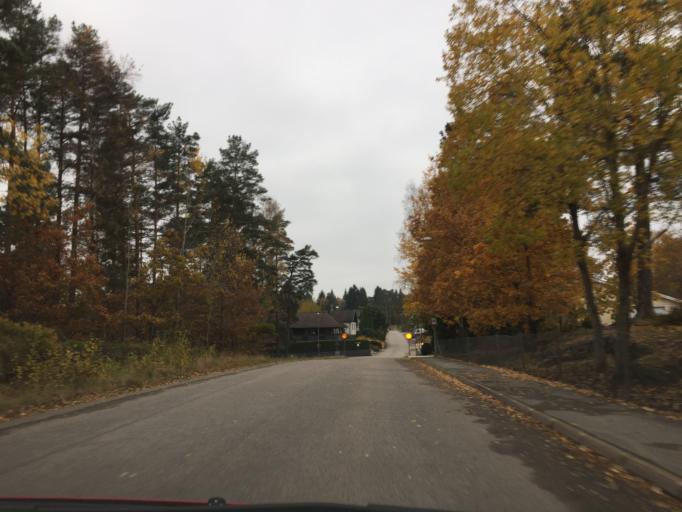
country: SE
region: Vaestra Goetaland
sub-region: Trollhattan
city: Trollhattan
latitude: 58.2604
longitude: 12.2600
